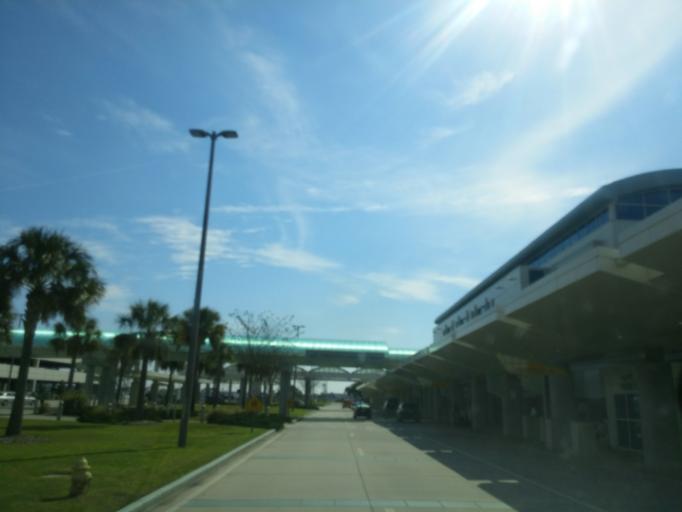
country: US
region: Mississippi
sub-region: Harrison County
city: West Gulfport
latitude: 30.4135
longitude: -89.0728
